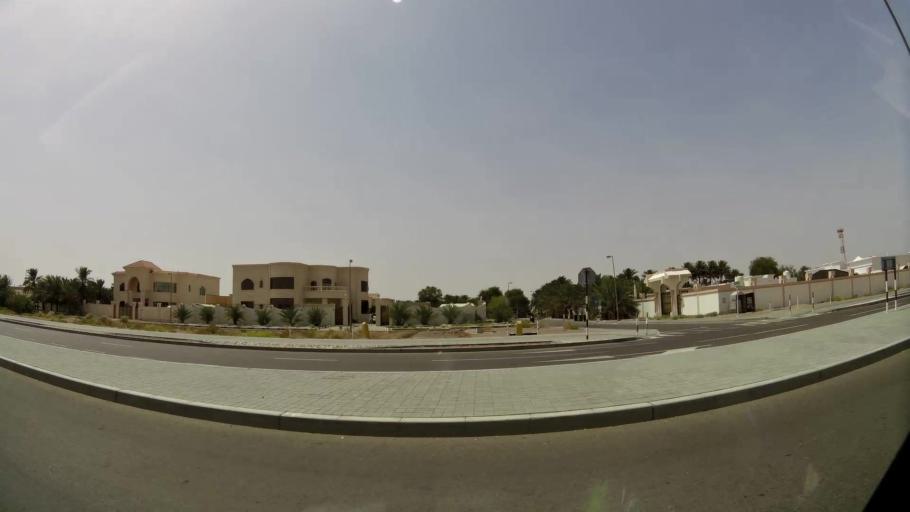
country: AE
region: Abu Dhabi
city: Al Ain
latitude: 24.1432
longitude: 55.6479
